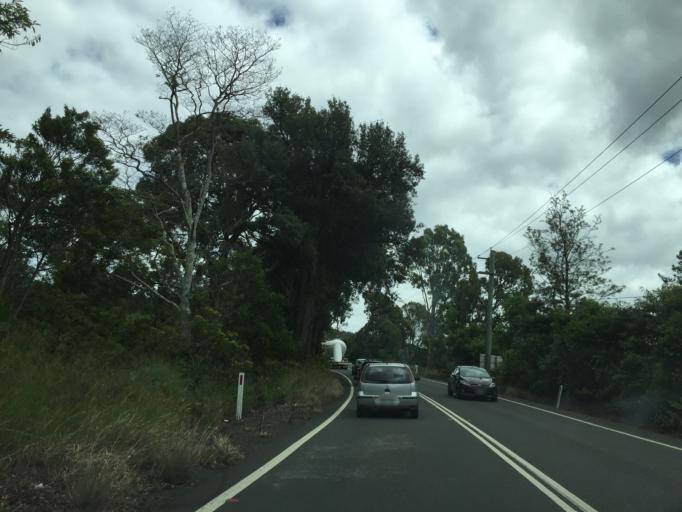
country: AU
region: New South Wales
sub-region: Hawkesbury
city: Richmond
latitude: -33.5456
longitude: 150.6487
